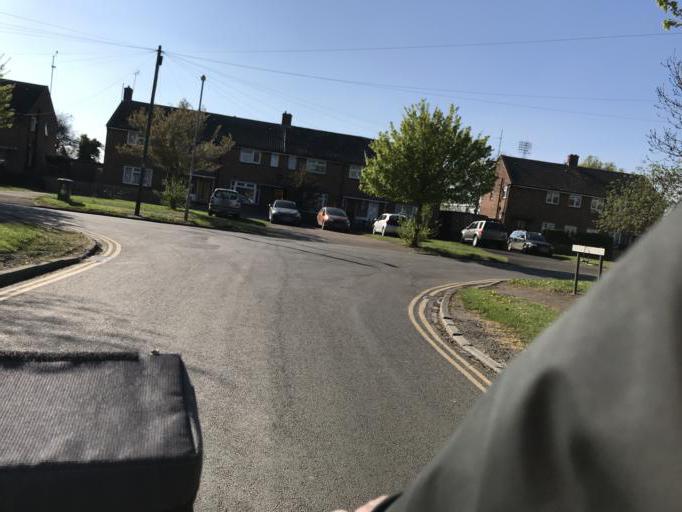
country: GB
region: England
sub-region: Cambridgeshire
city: Cambridge
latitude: 52.2103
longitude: 0.1572
